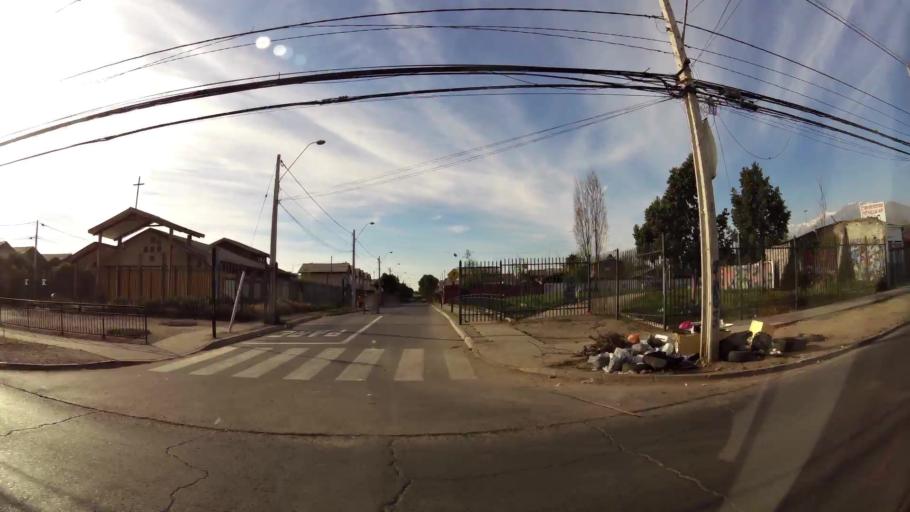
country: CL
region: Santiago Metropolitan
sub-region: Provincia de Cordillera
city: Puente Alto
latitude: -33.6134
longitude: -70.5849
